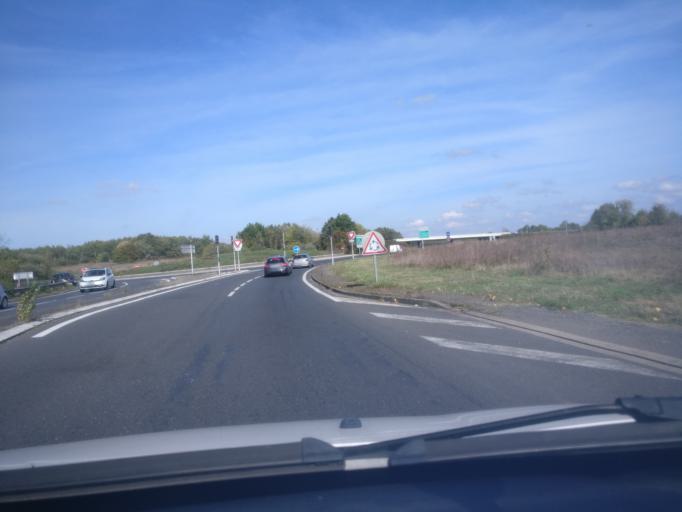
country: FR
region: Pays de la Loire
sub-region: Departement de la Loire-Atlantique
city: Sainte-Luce-sur-Loire
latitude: 47.2349
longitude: -1.4831
